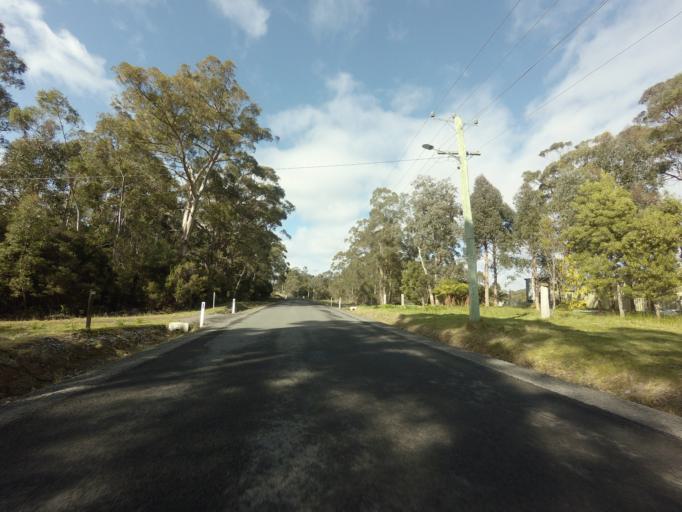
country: AU
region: Tasmania
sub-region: Huon Valley
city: Geeveston
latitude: -43.4322
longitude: 146.9035
